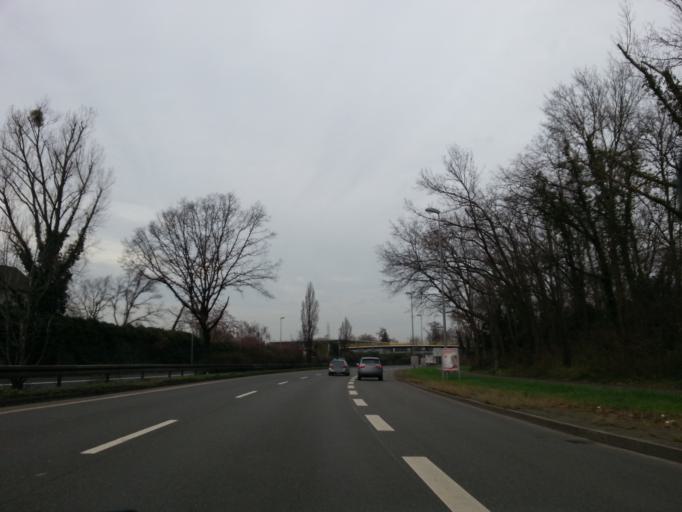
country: DE
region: North Rhine-Westphalia
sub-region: Regierungsbezirk Dusseldorf
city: Dusseldorf
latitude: 51.2571
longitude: 6.7630
